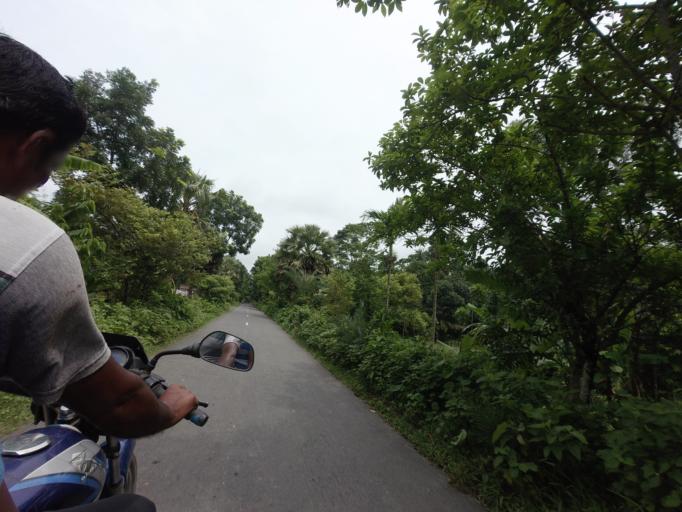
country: BD
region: Khulna
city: Kalia
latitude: 23.0876
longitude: 89.6624
